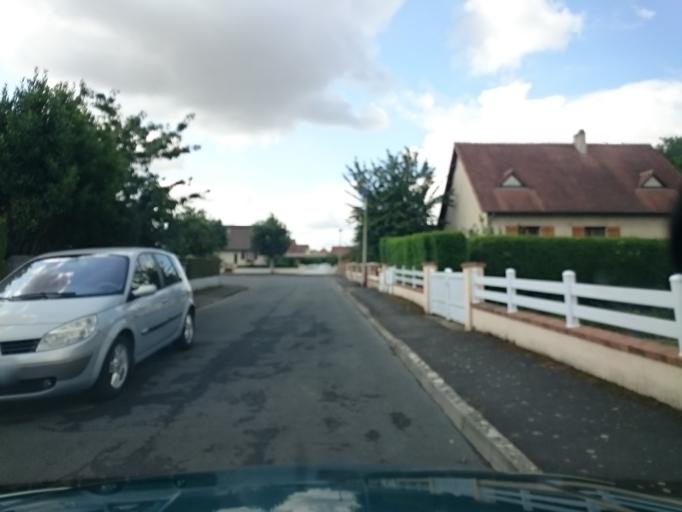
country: FR
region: Lower Normandy
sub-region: Departement du Calvados
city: Ifs
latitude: 49.1409
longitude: -0.3588
